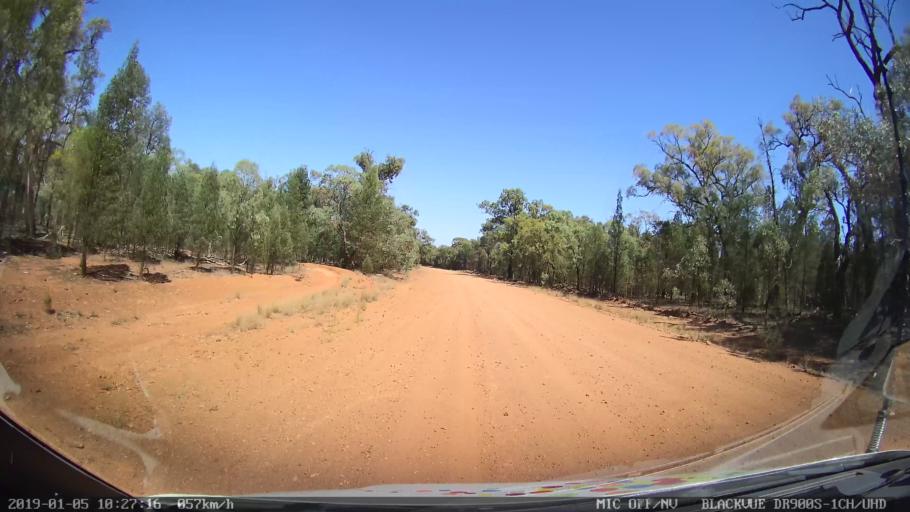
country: AU
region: New South Wales
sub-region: Gilgandra
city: Gilgandra
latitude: -31.5505
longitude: 148.9483
